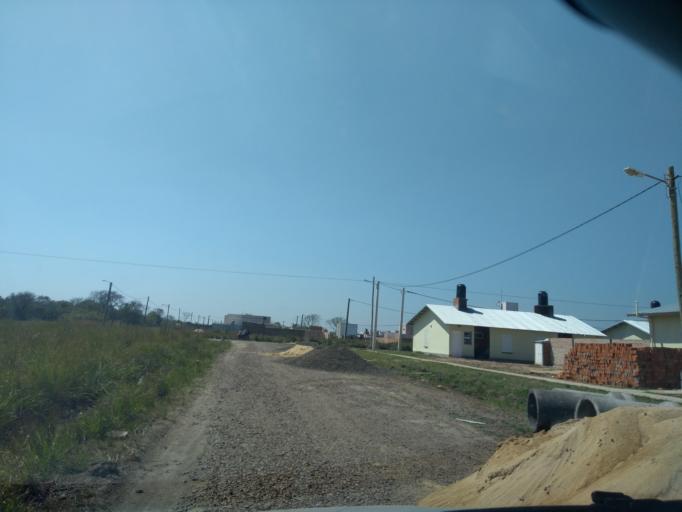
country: AR
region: Chaco
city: Fontana
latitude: -27.4066
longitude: -58.9751
